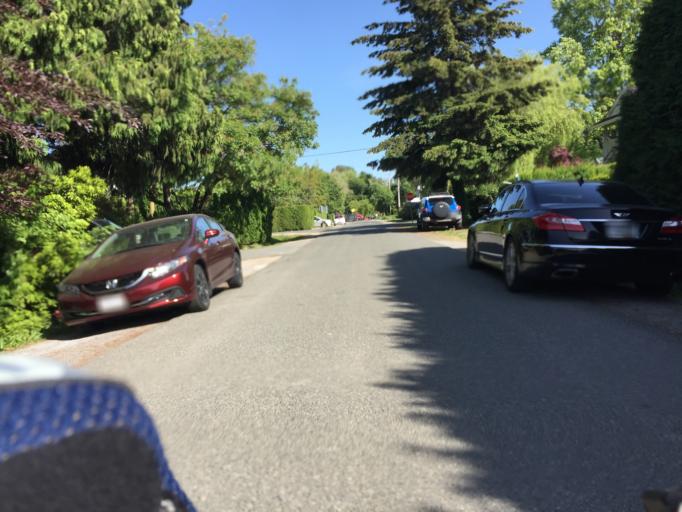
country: CA
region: British Columbia
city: Richmond
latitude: 49.1899
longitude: -123.1478
